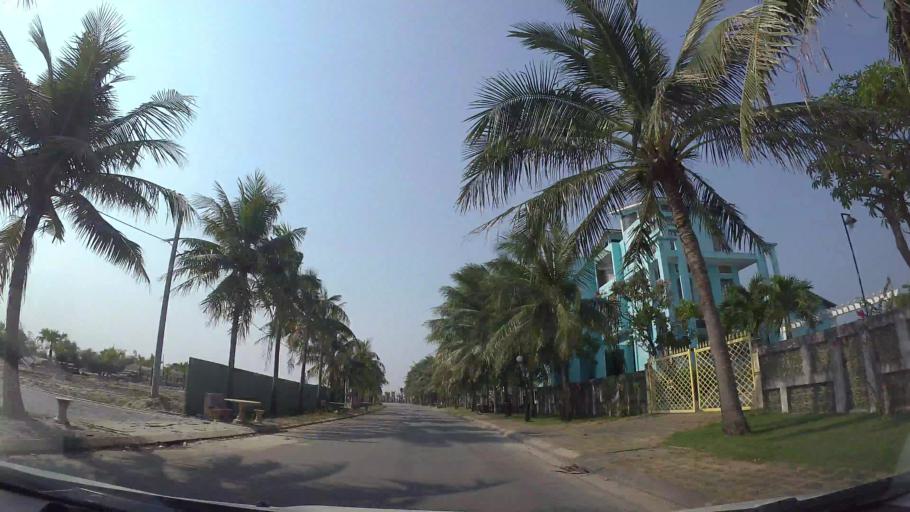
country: VN
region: Da Nang
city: Ngu Hanh Son
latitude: 15.9563
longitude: 108.2793
